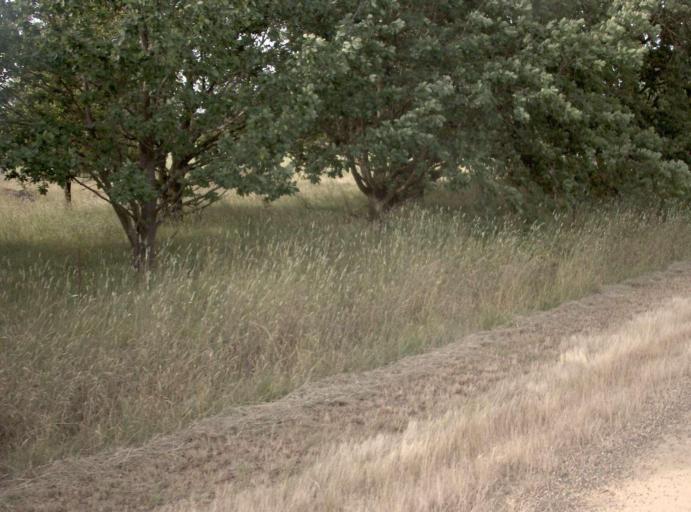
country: AU
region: Victoria
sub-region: Wellington
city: Heyfield
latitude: -38.0175
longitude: 146.7702
